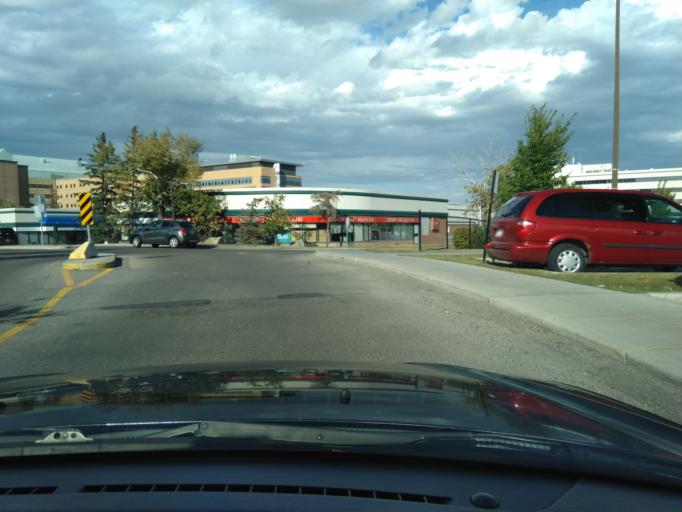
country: CA
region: Alberta
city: Calgary
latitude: 51.0768
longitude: -113.9855
